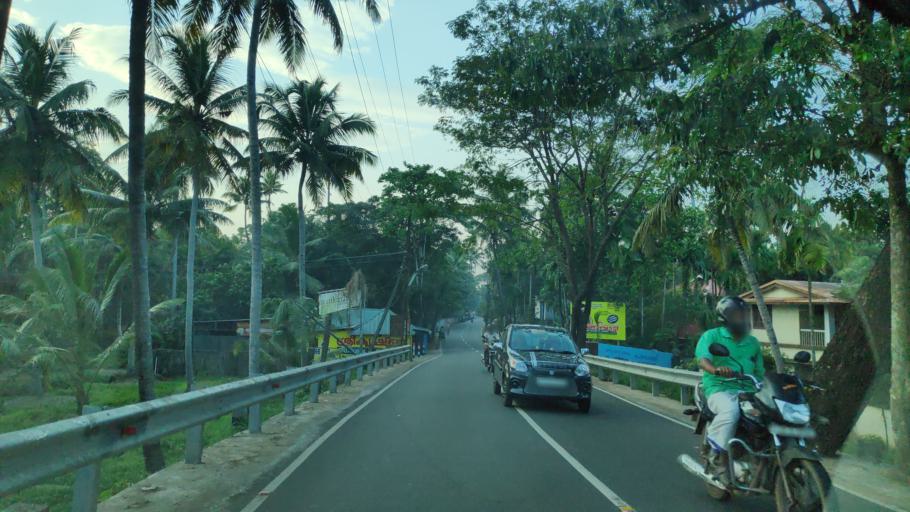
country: IN
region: Kerala
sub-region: Alappuzha
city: Shertallai
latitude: 9.6776
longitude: 76.3782
